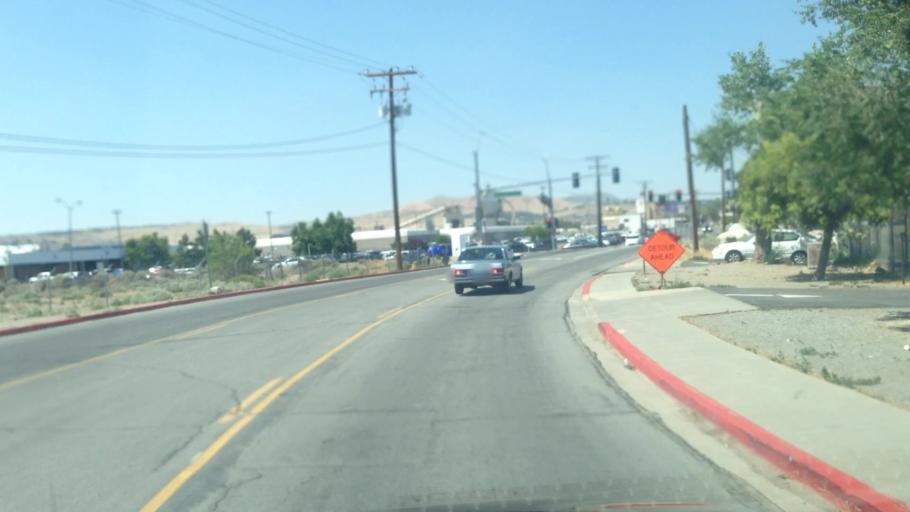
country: US
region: Nevada
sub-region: Washoe County
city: Sparks
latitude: 39.5308
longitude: -119.7803
